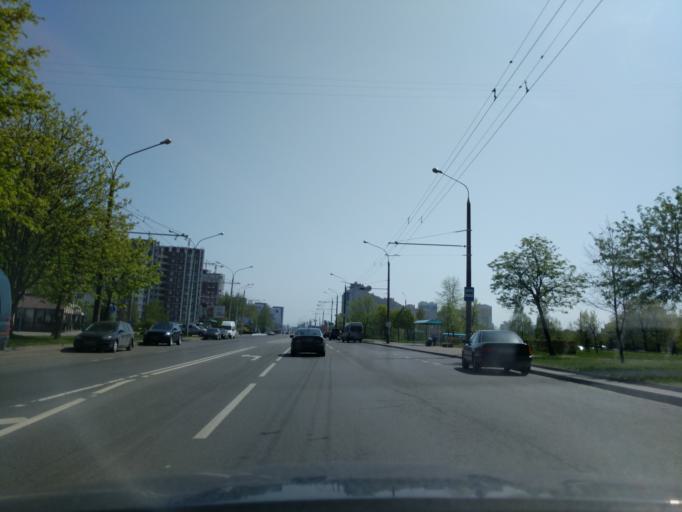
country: BY
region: Minsk
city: Novoye Medvezhino
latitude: 53.8591
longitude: 27.4683
